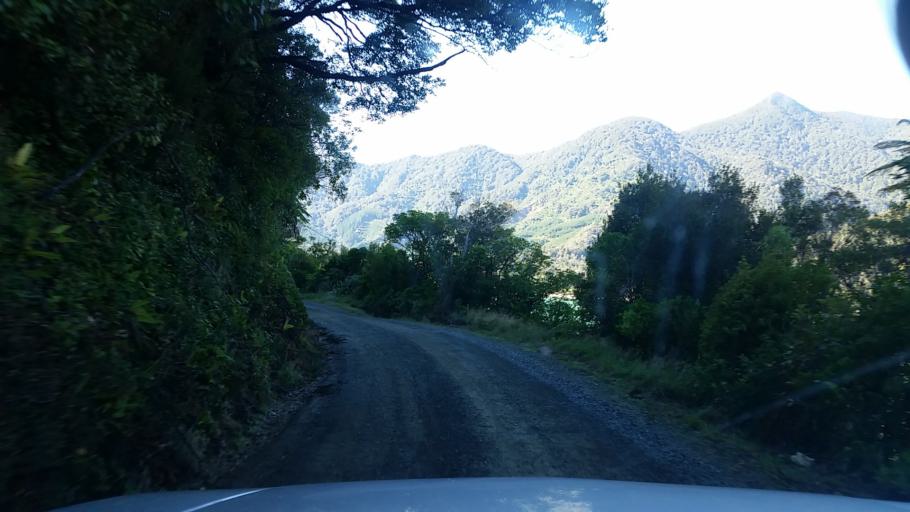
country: NZ
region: Marlborough
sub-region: Marlborough District
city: Picton
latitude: -41.1043
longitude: 173.6563
